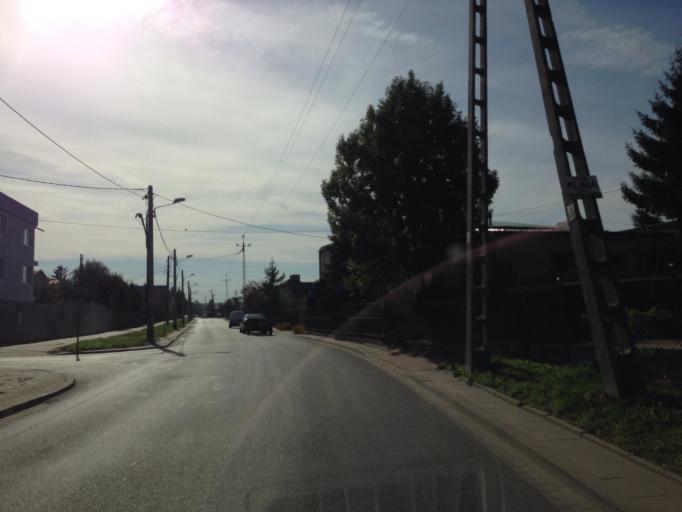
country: PL
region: Masovian Voivodeship
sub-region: Warszawa
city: Wlochy
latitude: 52.1814
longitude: 20.9400
